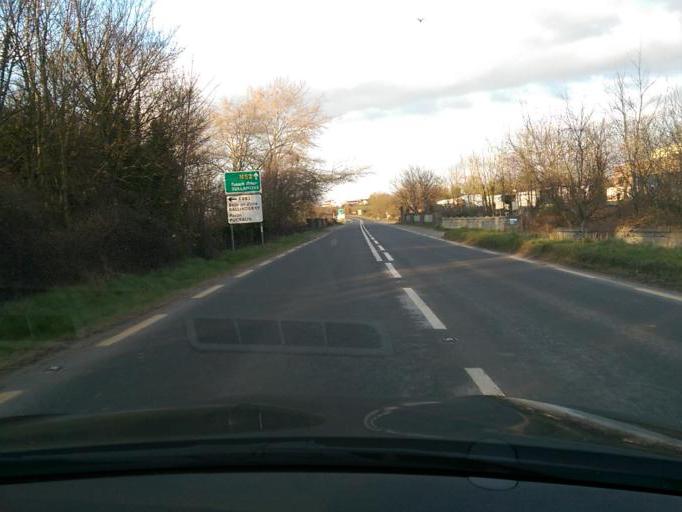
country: IE
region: Munster
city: Nenagh Bridge
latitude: 52.8819
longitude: -8.1984
